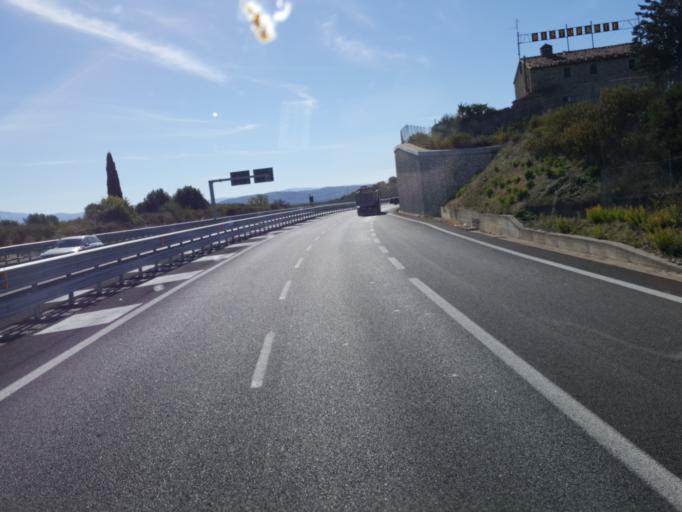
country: IT
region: Tuscany
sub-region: Provincia di Grosseto
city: Civitella Marittima
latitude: 42.9952
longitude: 11.2888
